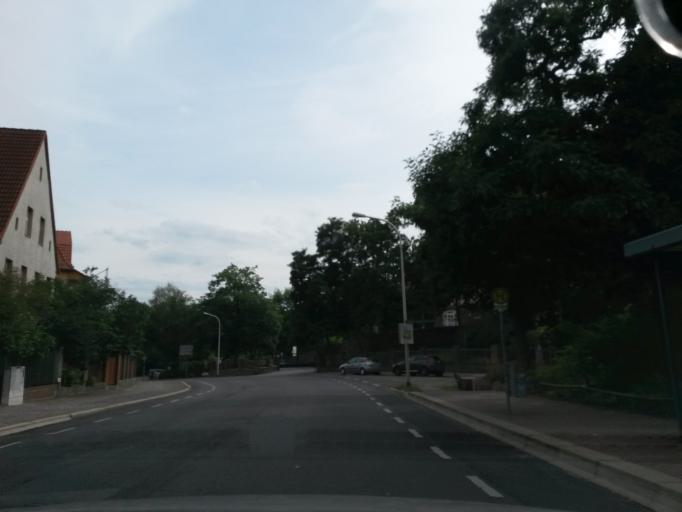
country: DE
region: Brandenburg
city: Eberswalde
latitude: 52.8309
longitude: 13.8054
